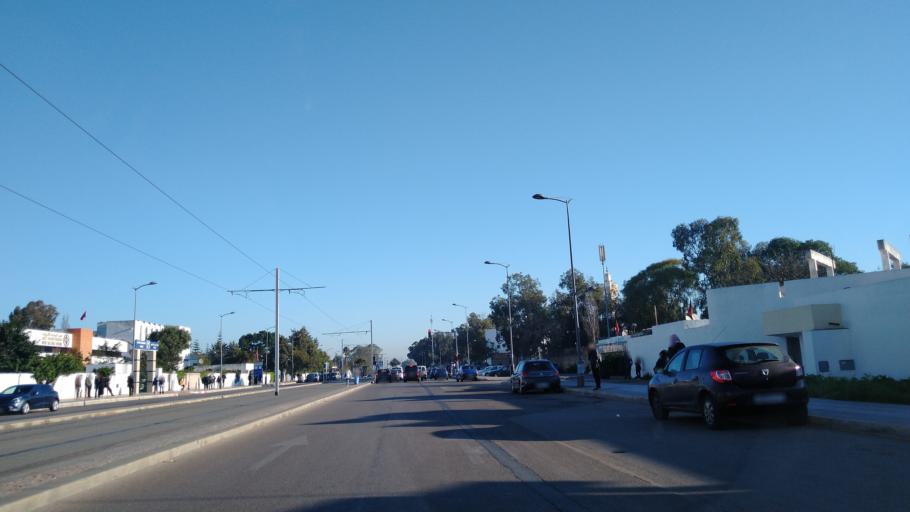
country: MA
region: Rabat-Sale-Zemmour-Zaer
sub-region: Rabat
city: Rabat
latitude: 33.9844
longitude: -6.8625
